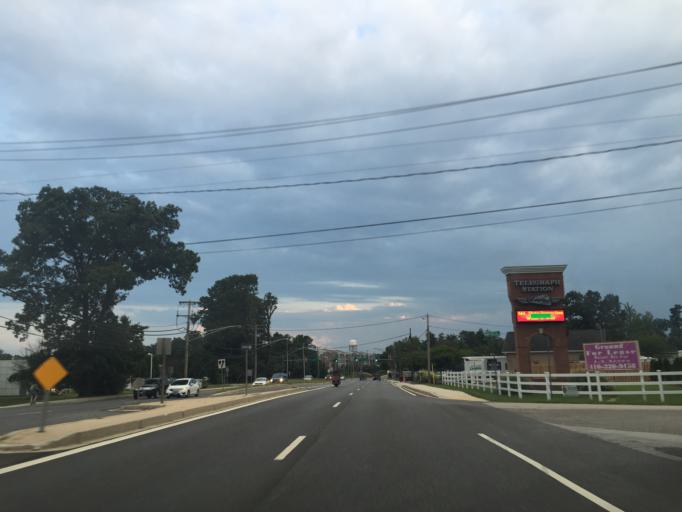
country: US
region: Maryland
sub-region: Anne Arundel County
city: Odenton
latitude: 39.0969
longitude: -76.6949
